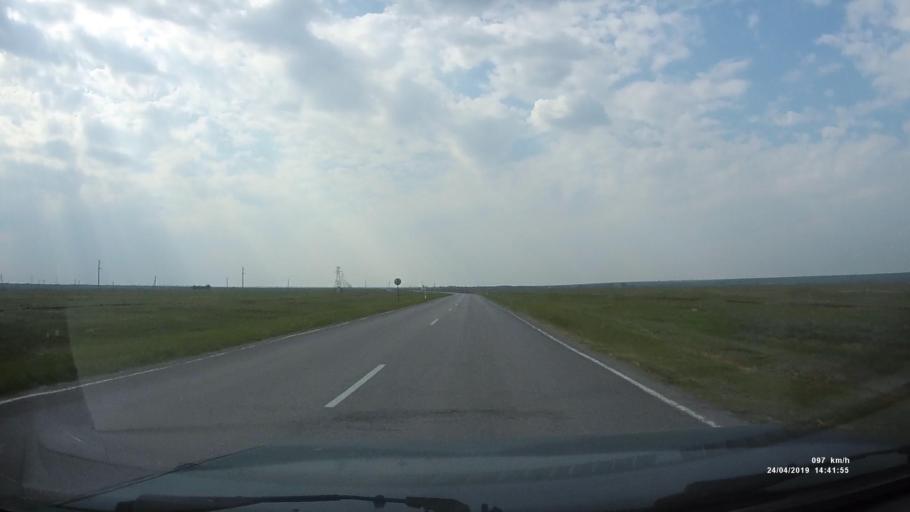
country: RU
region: Rostov
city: Remontnoye
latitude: 46.4491
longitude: 43.8719
